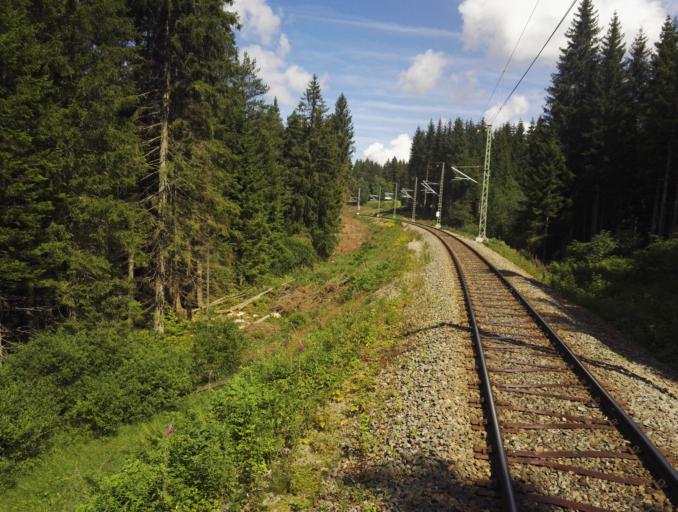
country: DE
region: Baden-Wuerttemberg
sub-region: Freiburg Region
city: Schluchsee
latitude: 47.8418
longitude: 8.1303
